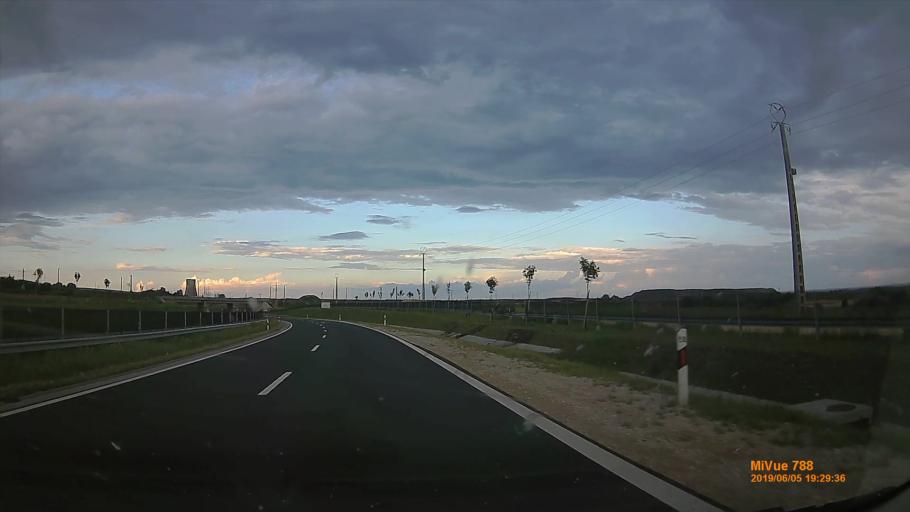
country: HU
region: Veszprem
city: Varpalota
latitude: 47.1950
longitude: 18.1777
